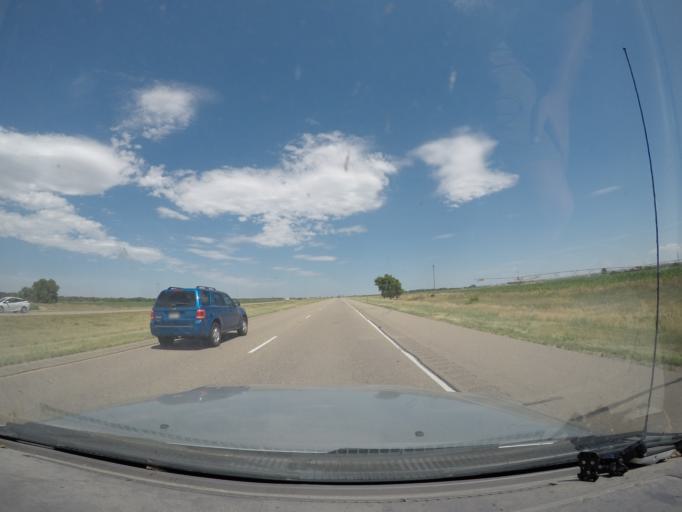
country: US
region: Colorado
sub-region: Sedgwick County
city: Julesburg
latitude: 41.0406
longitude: -102.1057
